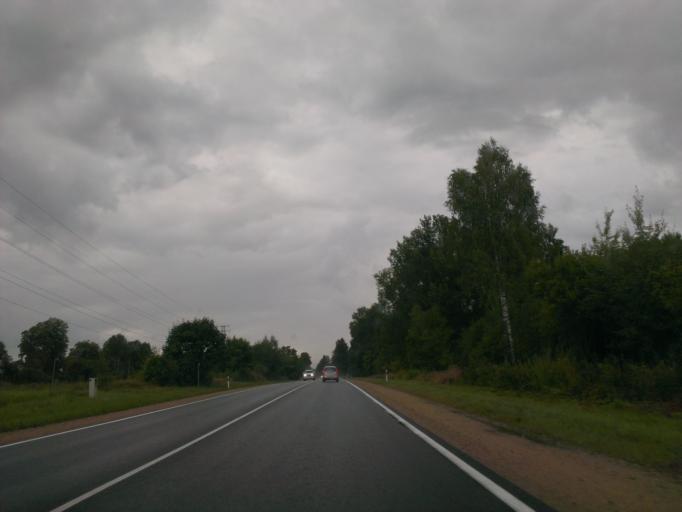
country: LV
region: Kegums
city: Kegums
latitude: 56.7572
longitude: 24.6997
